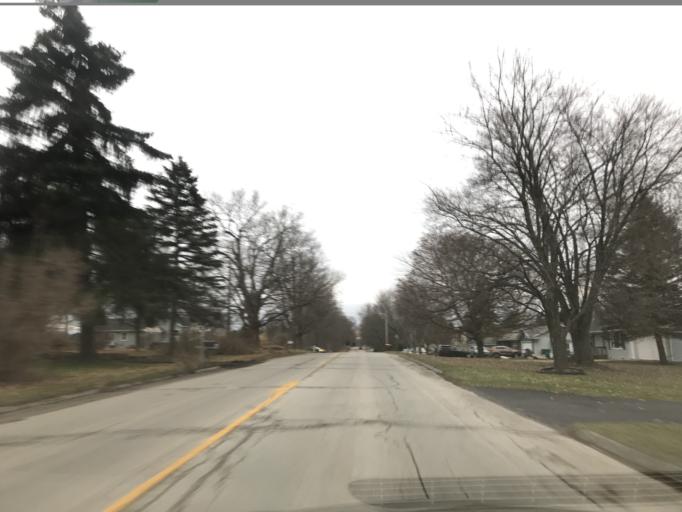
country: US
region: Michigan
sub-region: Eaton County
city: Dimondale
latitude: 42.6631
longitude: -84.6423
